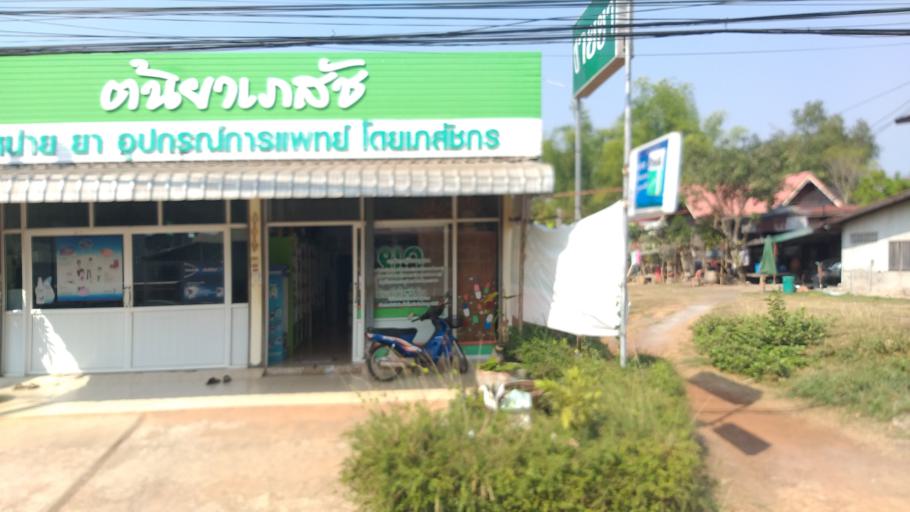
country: TH
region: Changwat Udon Thani
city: Nong Han
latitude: 17.3635
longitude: 103.1138
